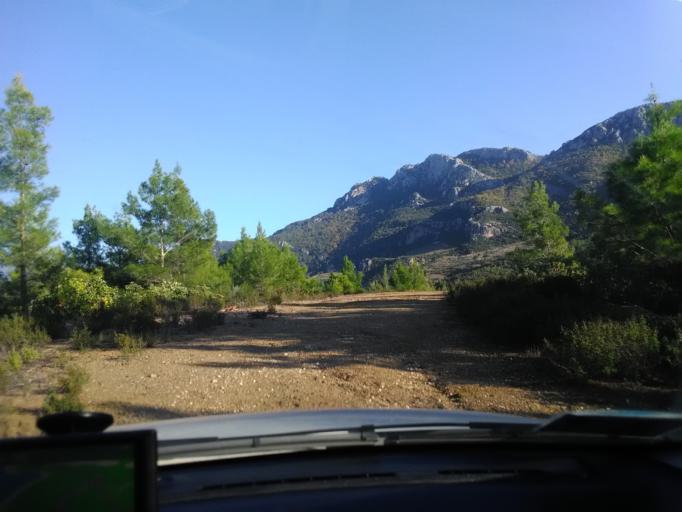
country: TR
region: Antalya
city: Gazipasa
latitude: 36.3088
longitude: 32.3950
